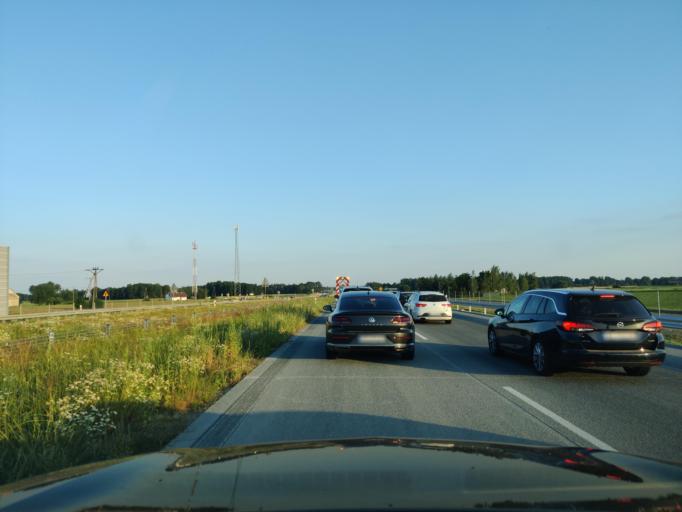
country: PL
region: Masovian Voivodeship
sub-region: Powiat plonski
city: Baboszewo
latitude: 52.7222
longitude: 20.3269
